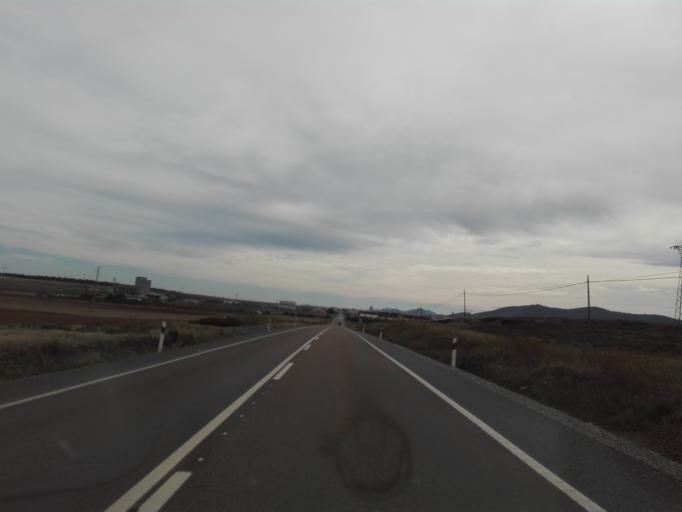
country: ES
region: Extremadura
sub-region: Provincia de Badajoz
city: Llerena
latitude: 38.2600
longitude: -6.0388
